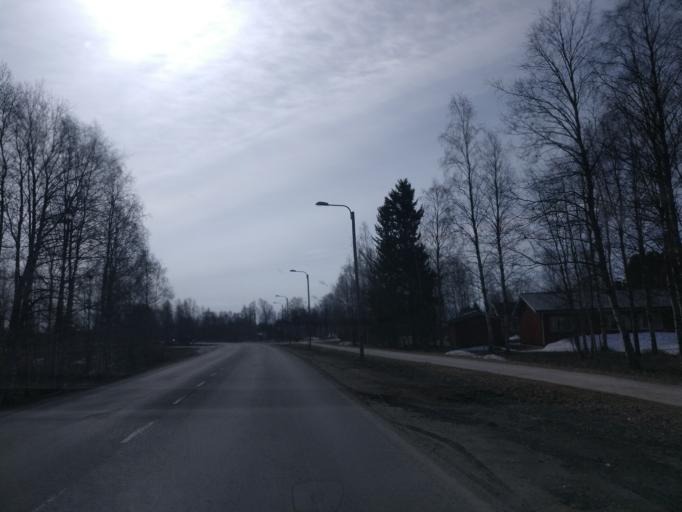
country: FI
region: Lapland
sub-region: Kemi-Tornio
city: Kemi
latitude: 65.7560
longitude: 24.5492
